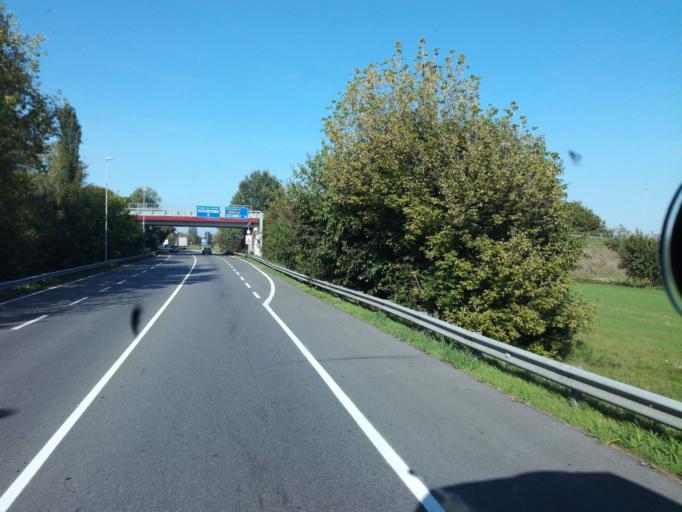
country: IT
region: Lombardy
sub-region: Provincia di Cremona
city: Crema
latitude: 45.3481
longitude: 9.6840
